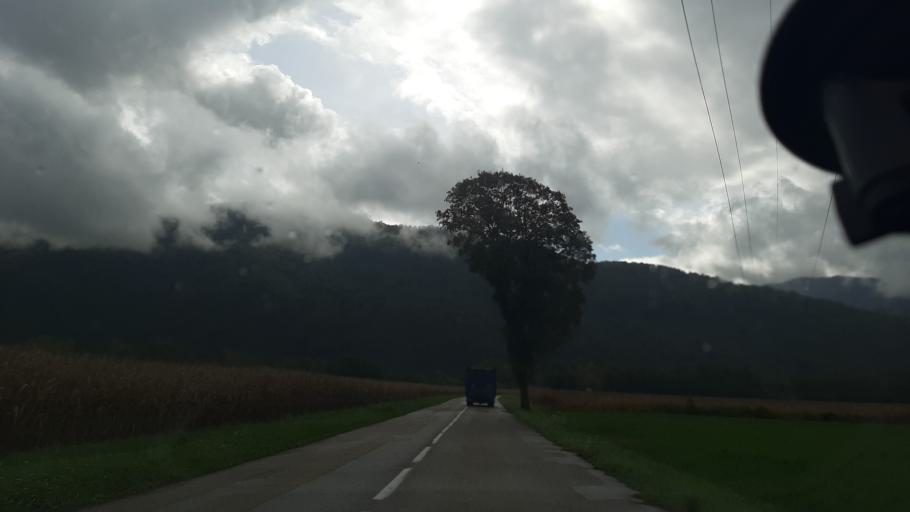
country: FR
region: Rhone-Alpes
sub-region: Departement de la Savoie
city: Gresy-sur-Isere
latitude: 45.5893
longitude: 6.2654
